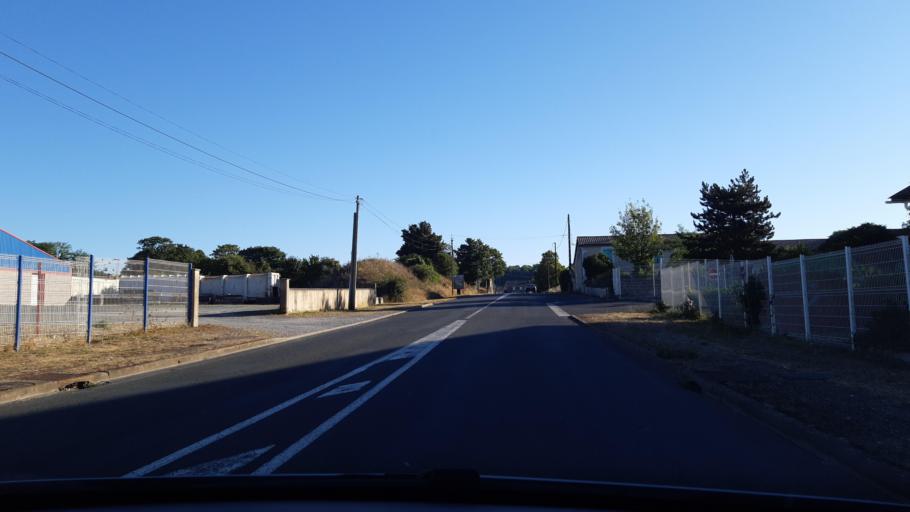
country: FR
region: Poitou-Charentes
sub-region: Departement des Deux-Sevres
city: Exireuil
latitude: 46.4257
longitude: -0.2044
